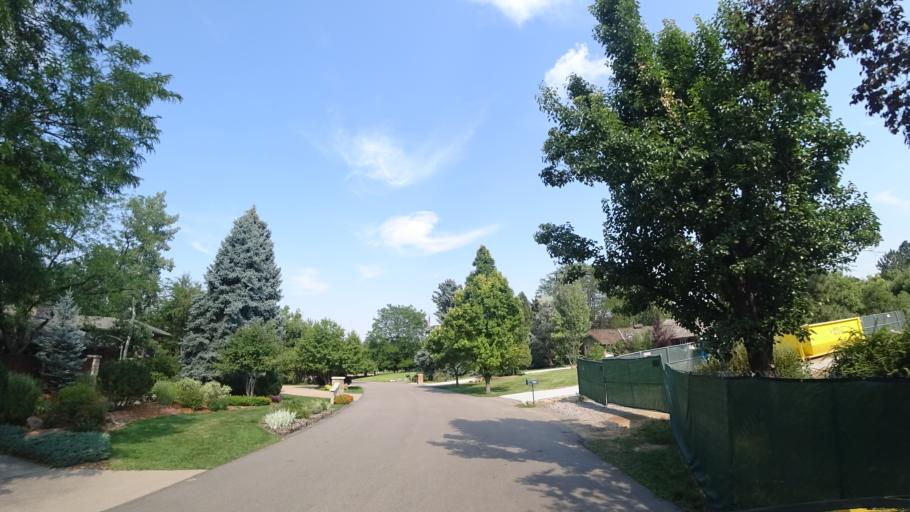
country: US
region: Colorado
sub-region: Arapahoe County
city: Greenwood Village
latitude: 39.6140
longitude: -104.9629
